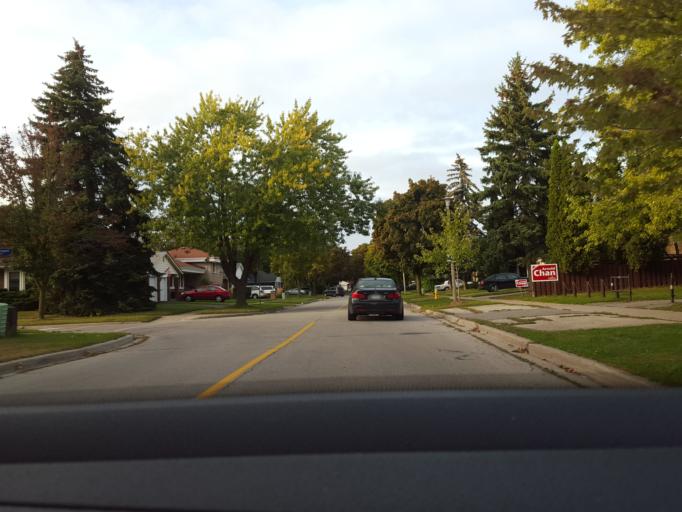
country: CA
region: Ontario
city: Scarborough
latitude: 43.7866
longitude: -79.3039
